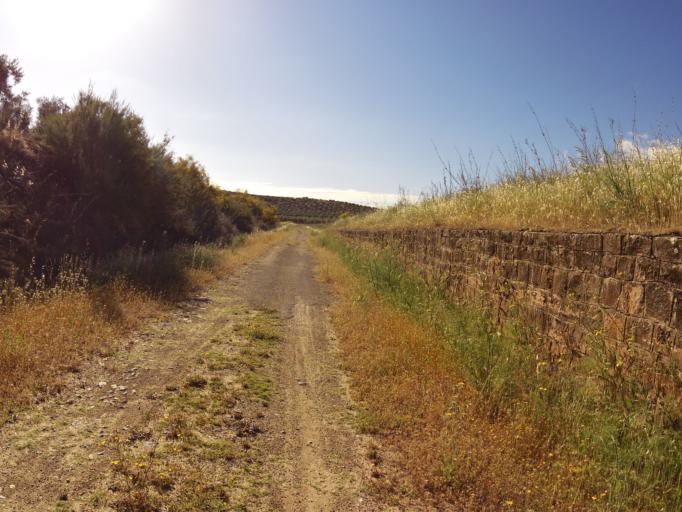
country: ES
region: Andalusia
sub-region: Province of Cordoba
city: Luque
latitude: 37.5829
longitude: -4.1983
